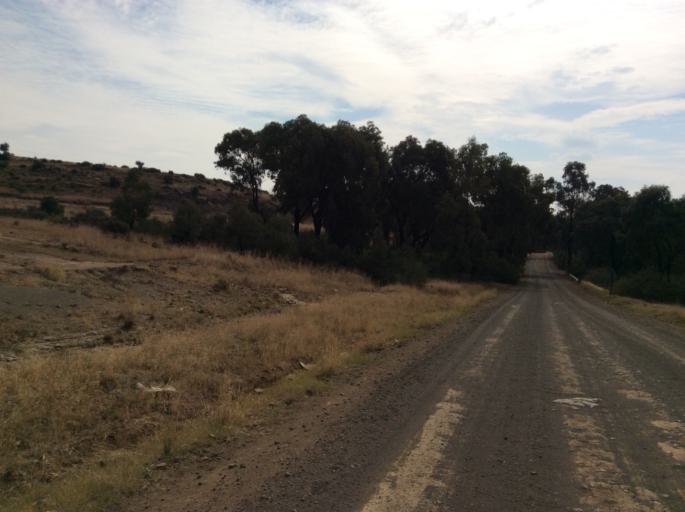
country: ZA
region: Orange Free State
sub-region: Xhariep District Municipality
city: Dewetsdorp
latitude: -29.5929
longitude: 26.6656
